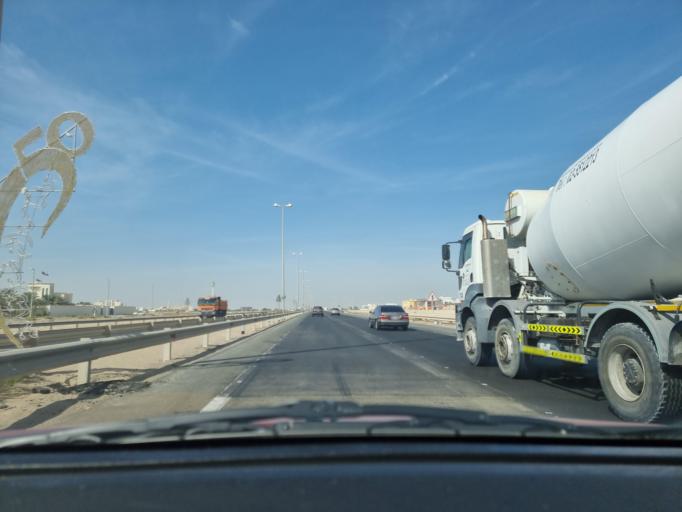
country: AE
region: Abu Dhabi
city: Abu Dhabi
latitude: 24.3611
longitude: 54.6659
